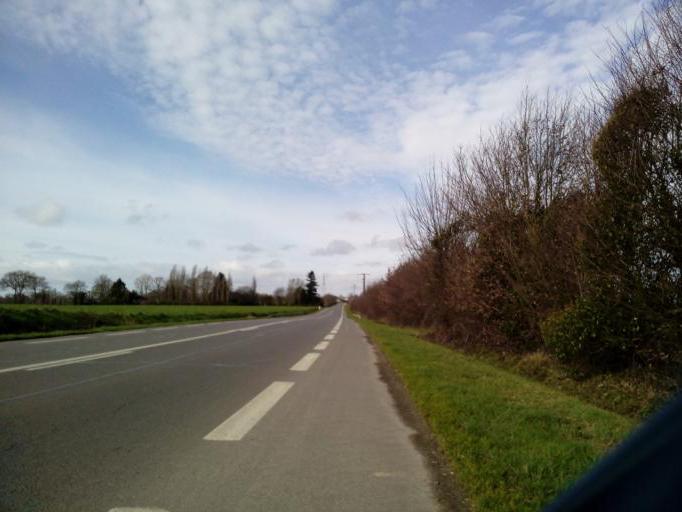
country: FR
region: Brittany
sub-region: Departement d'Ille-et-Vilaine
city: Montgermont
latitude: 48.1626
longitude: -1.7126
